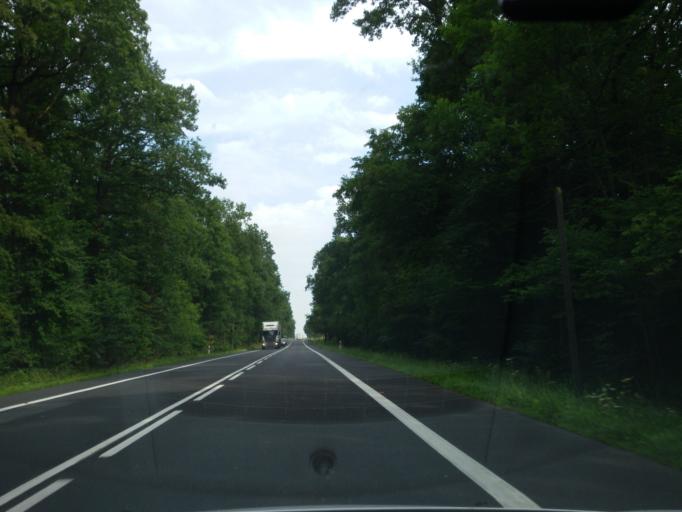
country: PL
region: Lubusz
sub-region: Powiat nowosolski
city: Bytom Odrzanski
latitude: 51.6672
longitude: 15.8061
